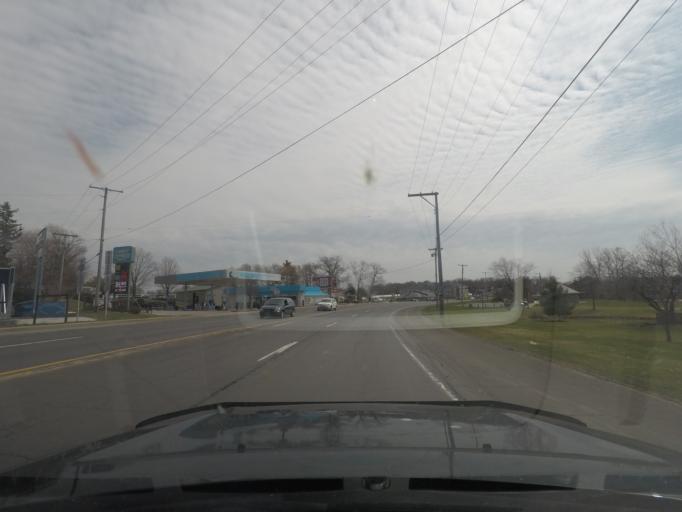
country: US
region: Indiana
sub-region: LaPorte County
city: LaPorte
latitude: 41.6320
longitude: -86.7393
